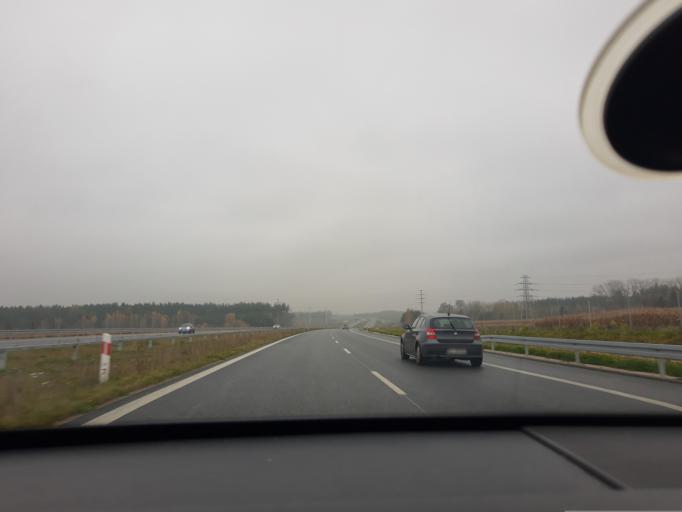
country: PL
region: Lodz Voivodeship
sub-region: Powiat pabianicki
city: Konstantynow Lodzki
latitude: 51.7089
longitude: 19.3437
